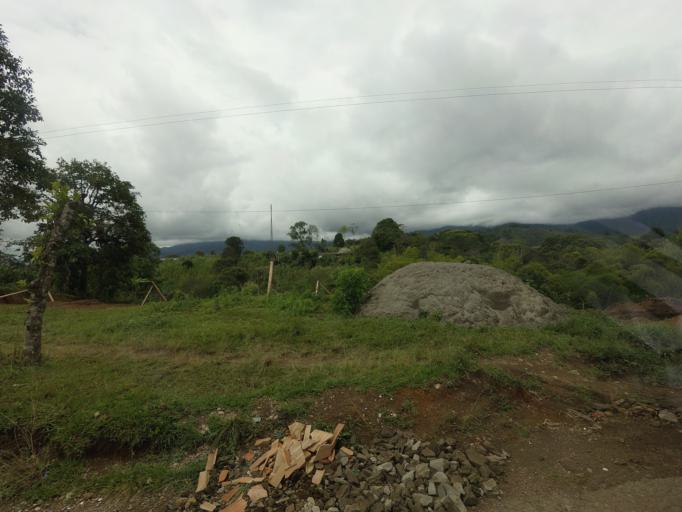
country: CO
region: Huila
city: San Agustin
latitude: 1.9381
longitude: -76.2987
